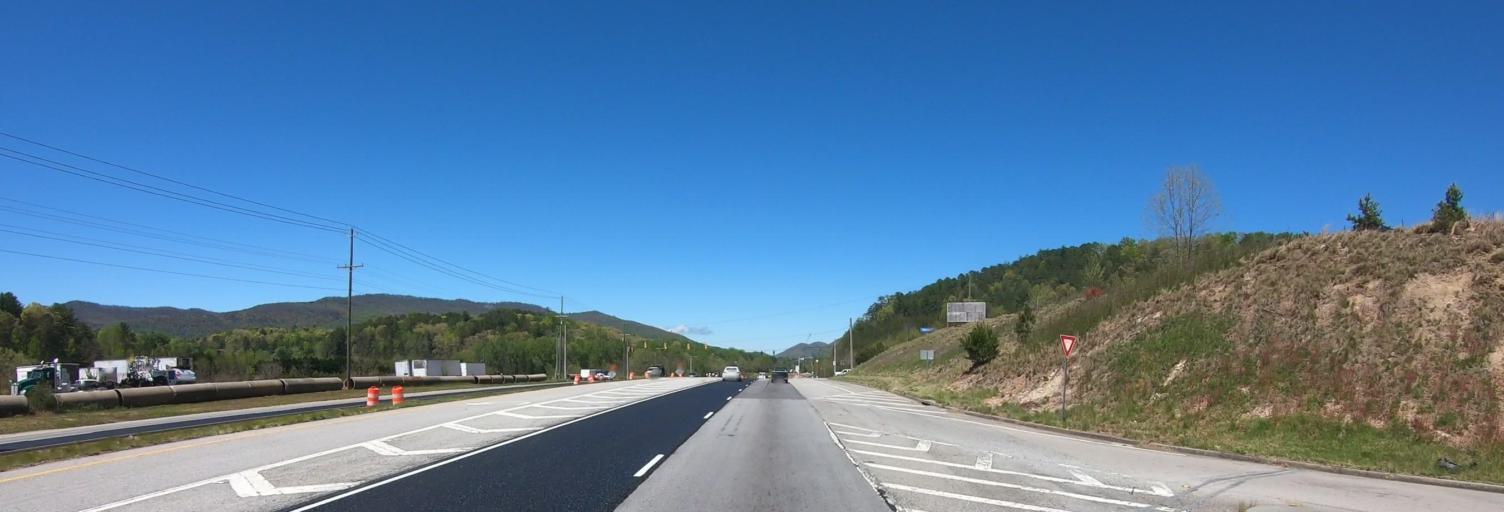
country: US
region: Georgia
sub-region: Rabun County
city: Clayton
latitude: 34.8585
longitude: -83.4054
